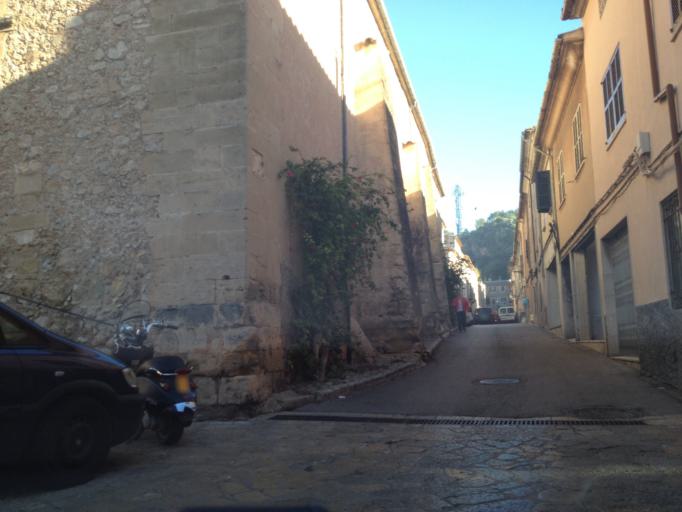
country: ES
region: Balearic Islands
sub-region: Illes Balears
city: Pollenca
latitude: 39.8792
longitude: 3.0181
